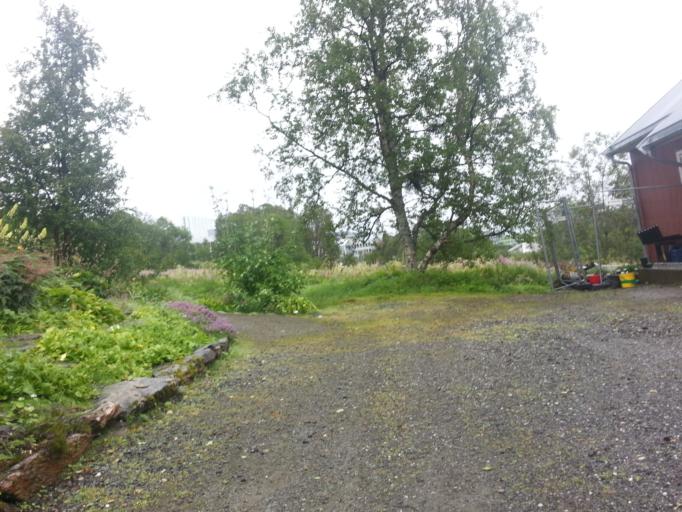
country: NO
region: Troms
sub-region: Tromso
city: Tromso
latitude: 69.6771
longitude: 18.9767
